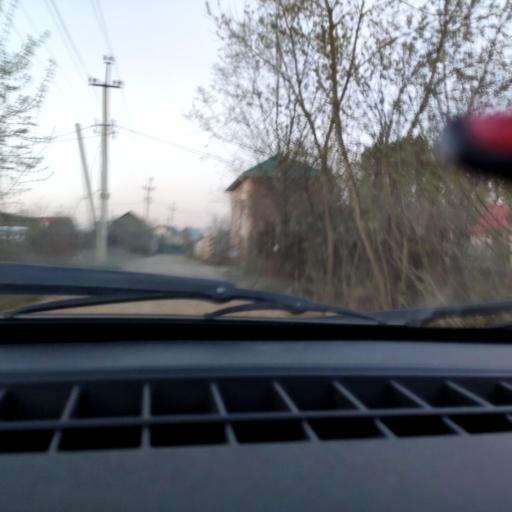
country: RU
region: Bashkortostan
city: Ufa
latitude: 54.6903
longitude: 55.8884
